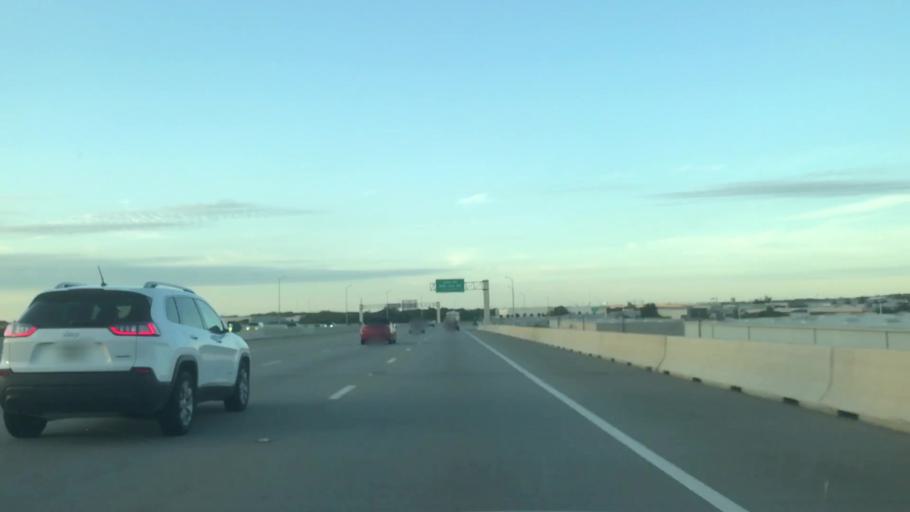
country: US
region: Texas
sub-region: Dallas County
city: Farmers Branch
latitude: 32.9389
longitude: -96.9298
